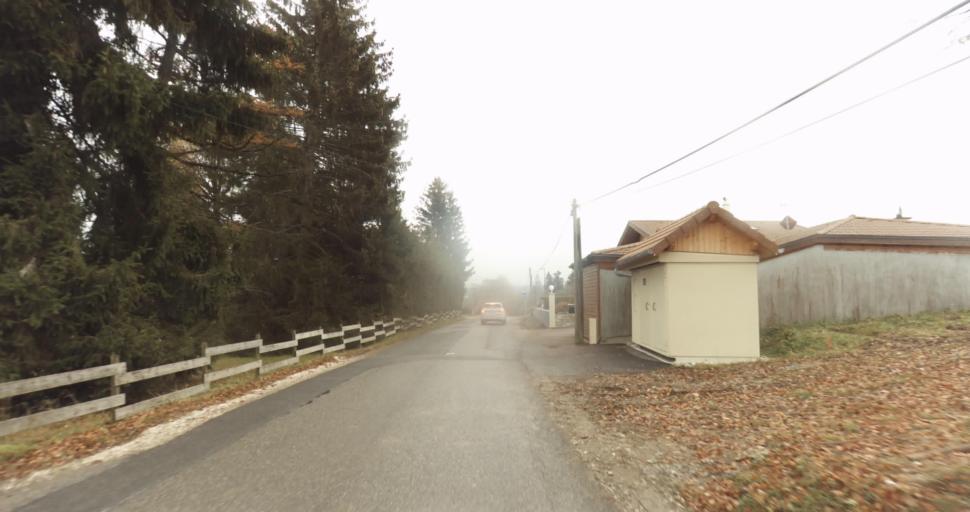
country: FR
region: Rhone-Alpes
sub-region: Departement de la Haute-Savoie
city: Evires
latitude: 46.0456
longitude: 6.2302
